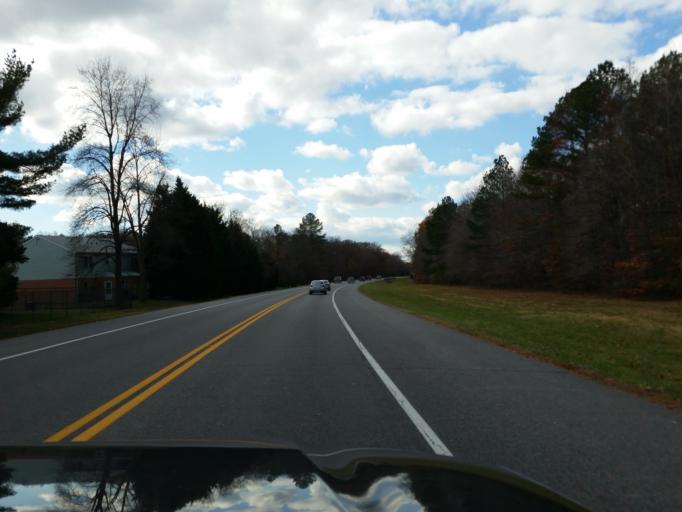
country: US
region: Maryland
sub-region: Talbot County
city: Easton
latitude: 38.7924
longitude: -76.0682
